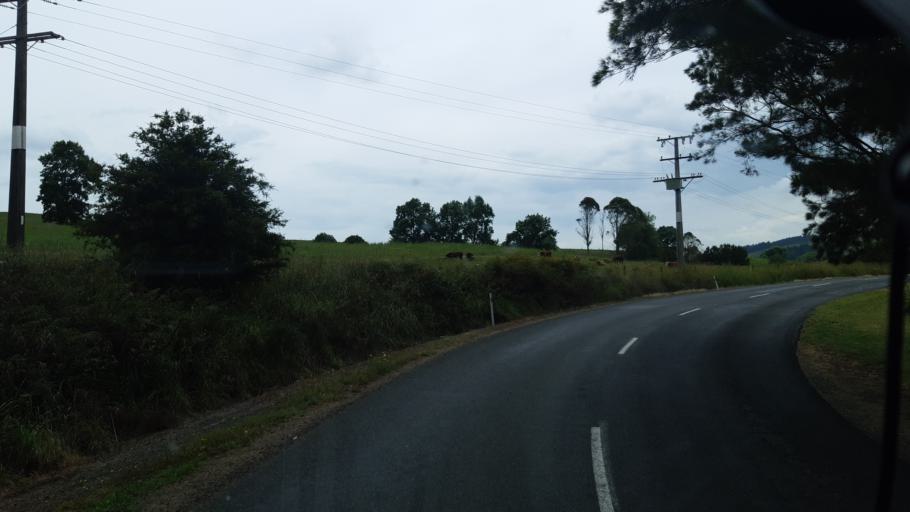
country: NZ
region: Waikato
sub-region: Waikato District
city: Raglan
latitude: -37.8444
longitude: 175.0274
